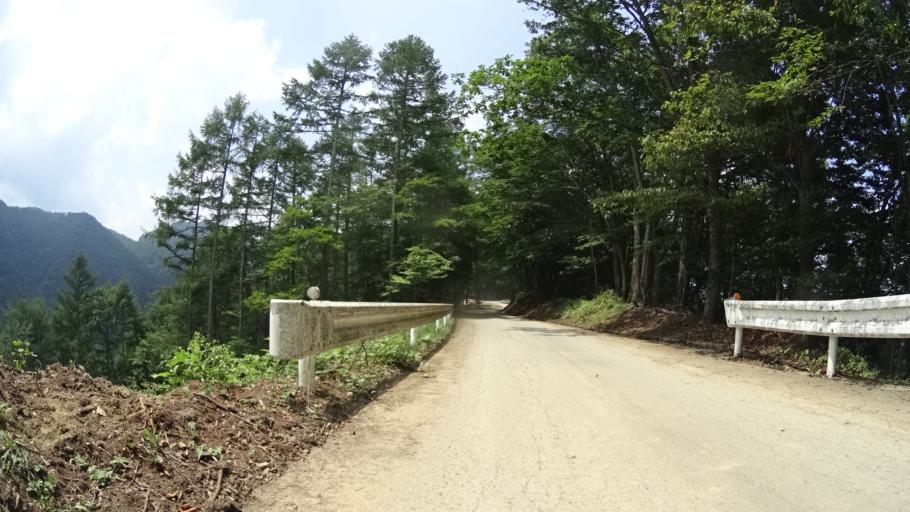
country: JP
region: Nagano
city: Saku
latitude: 36.0978
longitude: 138.6731
